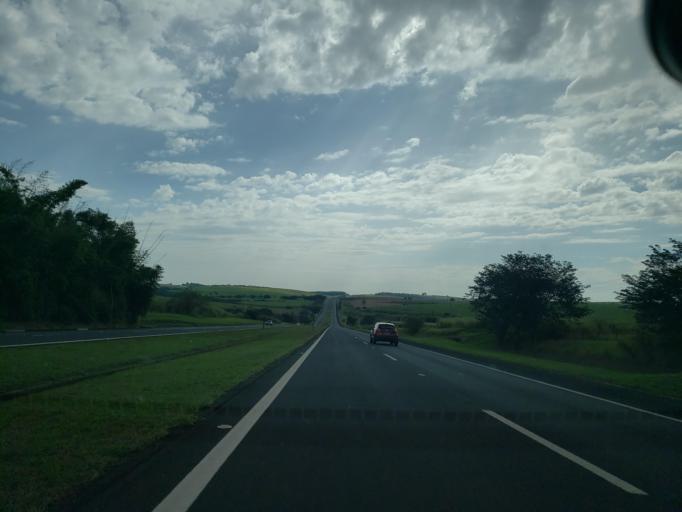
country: BR
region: Sao Paulo
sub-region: Lins
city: Lins
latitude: -21.7470
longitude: -49.6907
